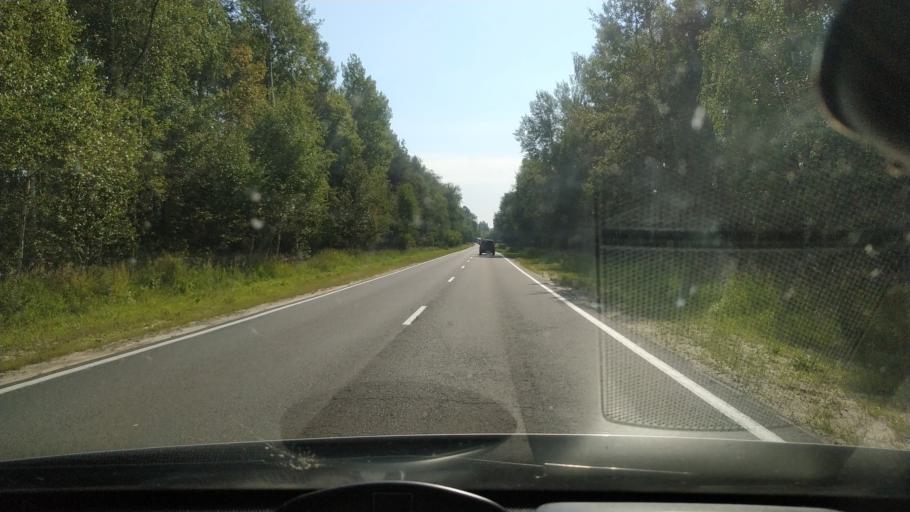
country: RU
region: Rjazan
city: Spas-Klepiki
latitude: 55.2212
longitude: 40.0847
